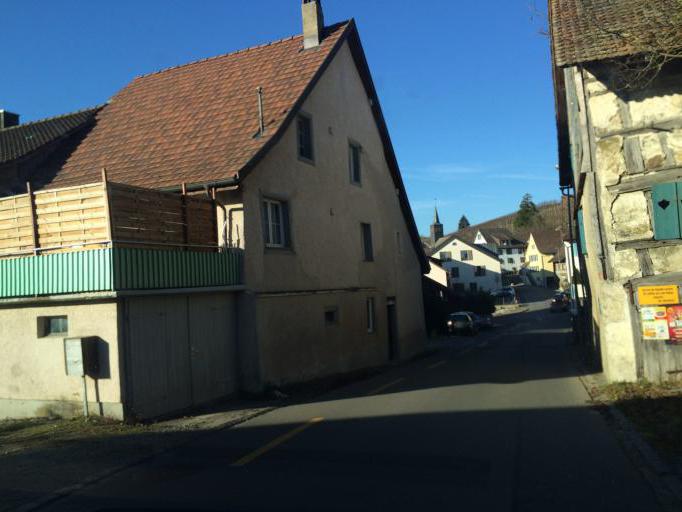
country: CH
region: Thurgau
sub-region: Frauenfeld District
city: Diessenhofen
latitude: 47.7044
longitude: 8.7247
